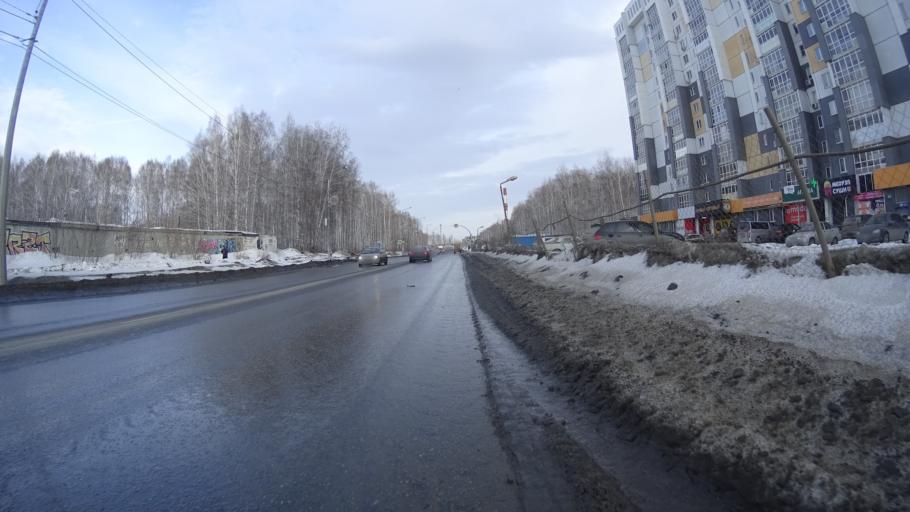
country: RU
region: Chelyabinsk
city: Roshchino
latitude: 55.2086
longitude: 61.3058
